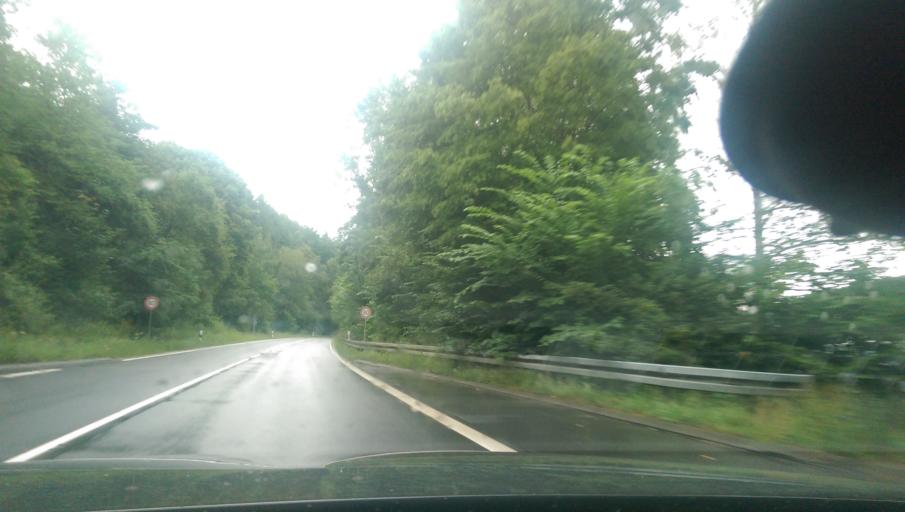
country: DE
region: Hesse
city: Witzenhausen
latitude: 51.3158
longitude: 9.8479
